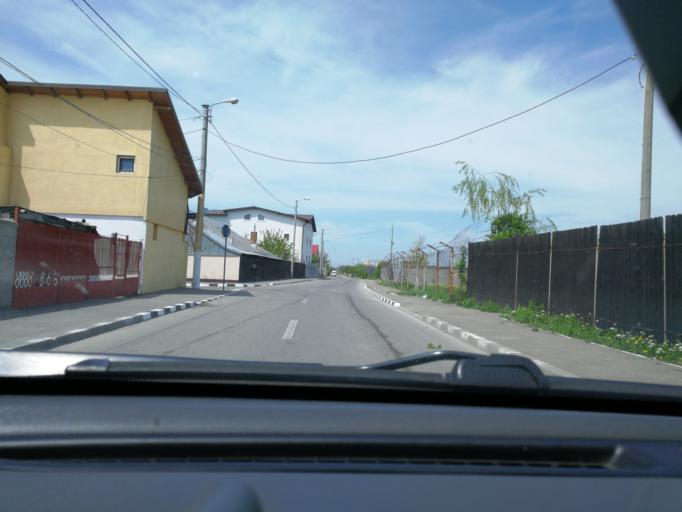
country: RO
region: Prahova
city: Ploiesti
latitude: 44.9503
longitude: 26.0516
